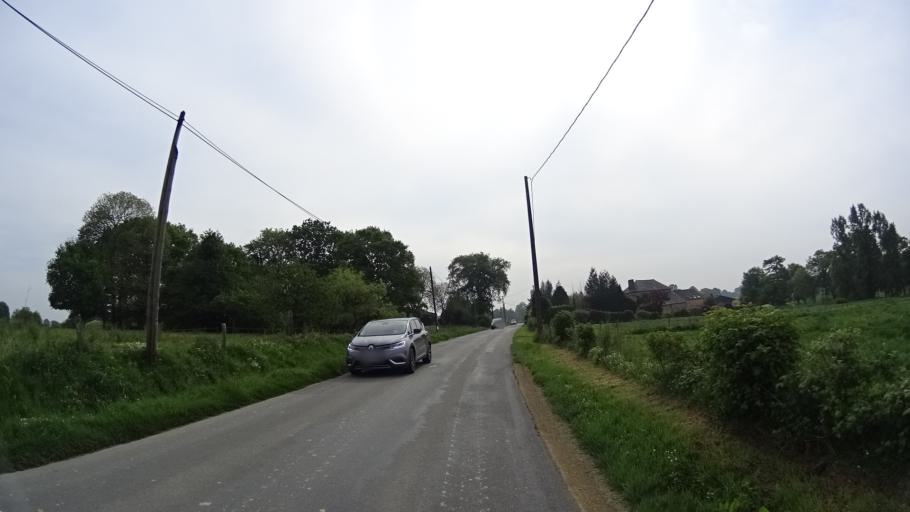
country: FR
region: Brittany
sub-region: Departement d'Ille-et-Vilaine
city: Montreuil-le-Gast
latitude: 48.2507
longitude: -1.7496
